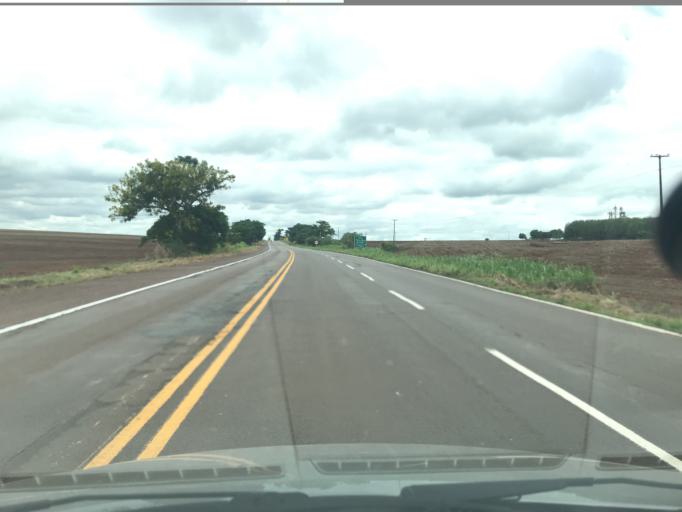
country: BR
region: Parana
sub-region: Terra Boa
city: Terra Boa
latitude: -23.5993
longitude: -52.3692
